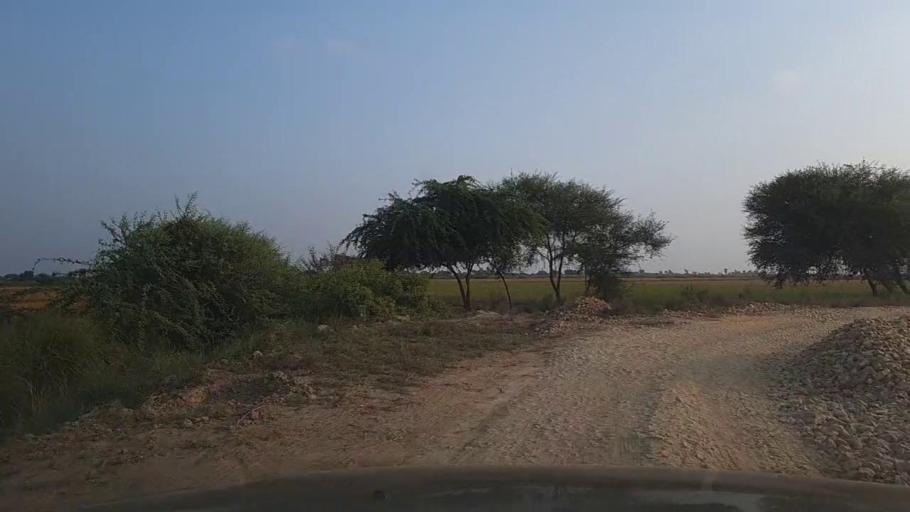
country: PK
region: Sindh
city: Jati
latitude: 24.5374
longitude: 68.3608
